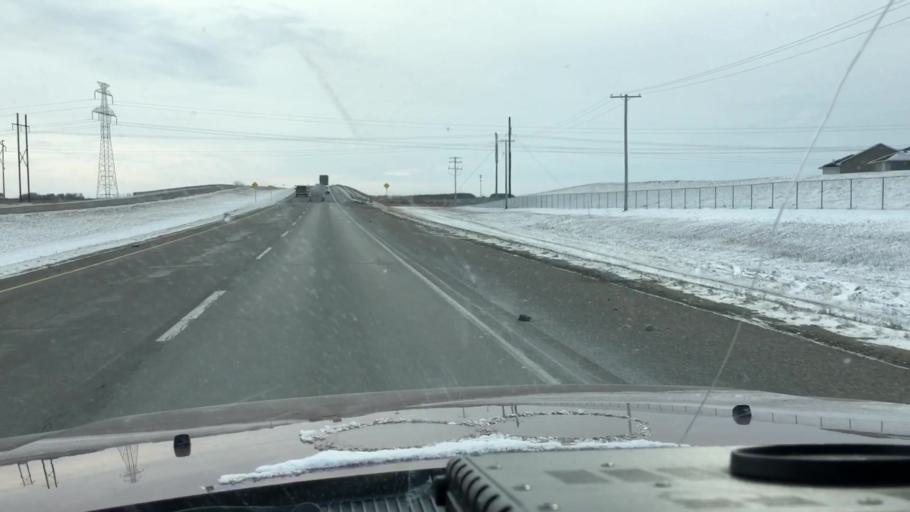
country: CA
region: Saskatchewan
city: Saskatoon
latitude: 52.0737
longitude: -106.6045
